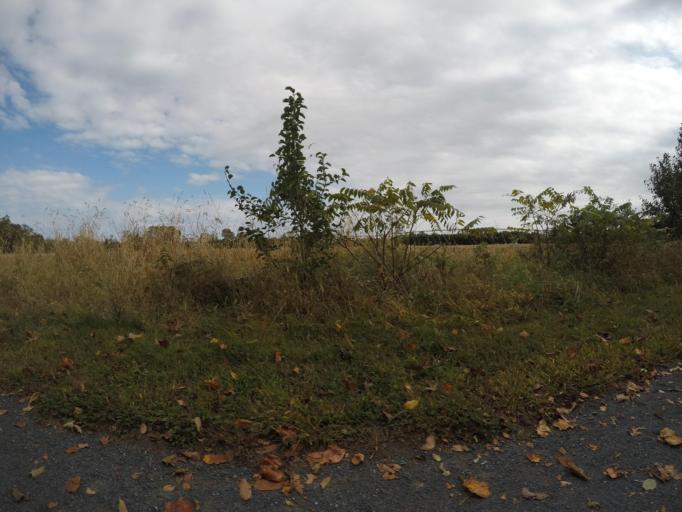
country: US
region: Delaware
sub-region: Sussex County
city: Rehoboth Beach
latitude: 38.7229
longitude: -75.1068
